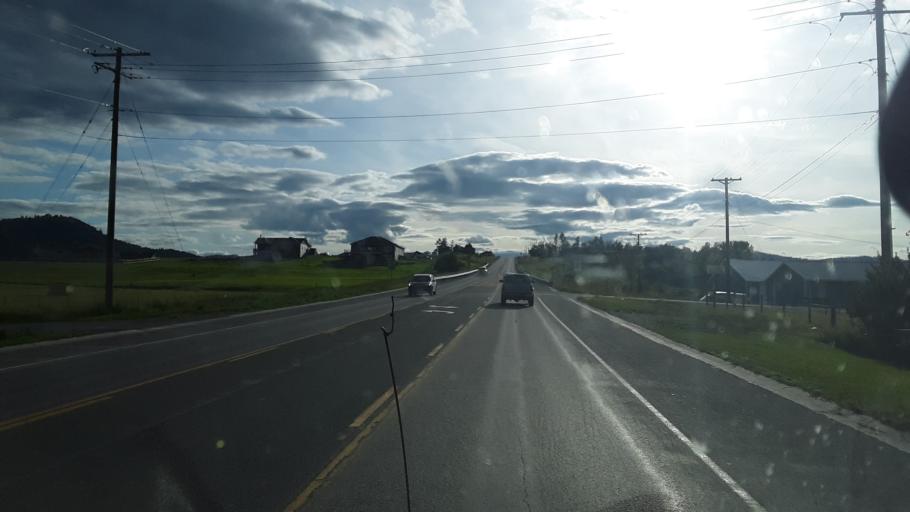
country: US
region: Montana
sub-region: Flathead County
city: Kalispell
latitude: 48.1967
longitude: -114.3453
